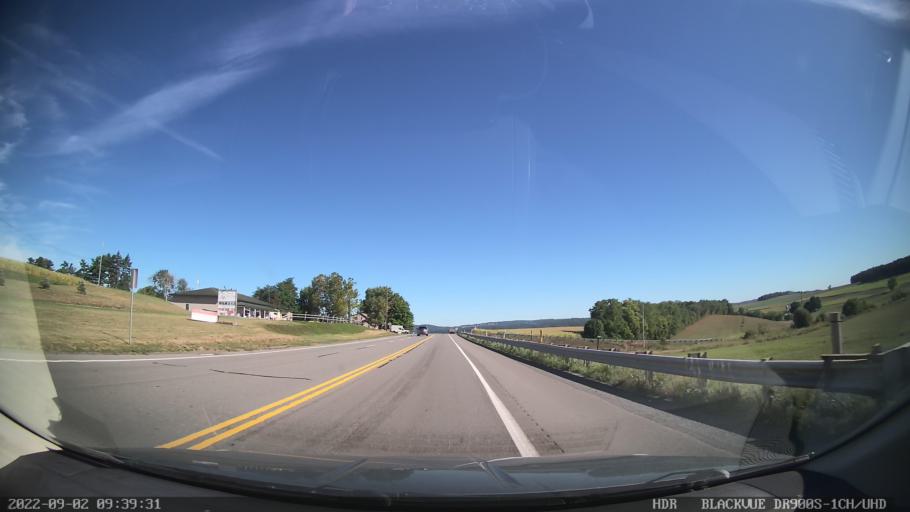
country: US
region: Pennsylvania
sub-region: Montour County
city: Mechanicsville
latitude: 40.9136
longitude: -76.5855
